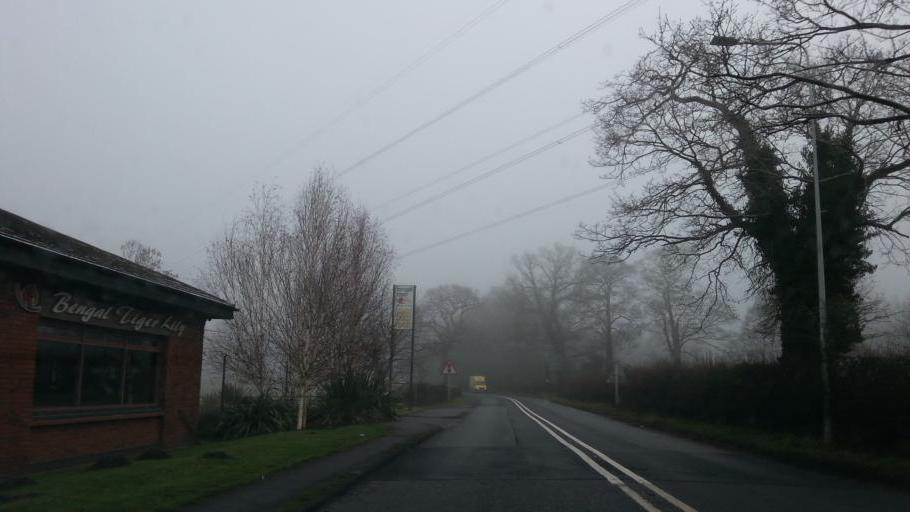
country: GB
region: England
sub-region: Cheshire East
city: Siddington
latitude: 53.2653
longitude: -2.2345
